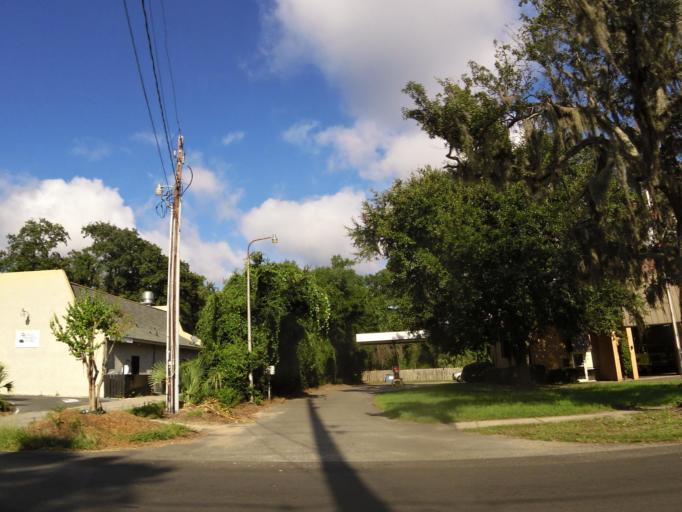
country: US
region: Georgia
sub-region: Glynn County
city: Saint Simon Mills
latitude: 31.1879
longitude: -81.3769
